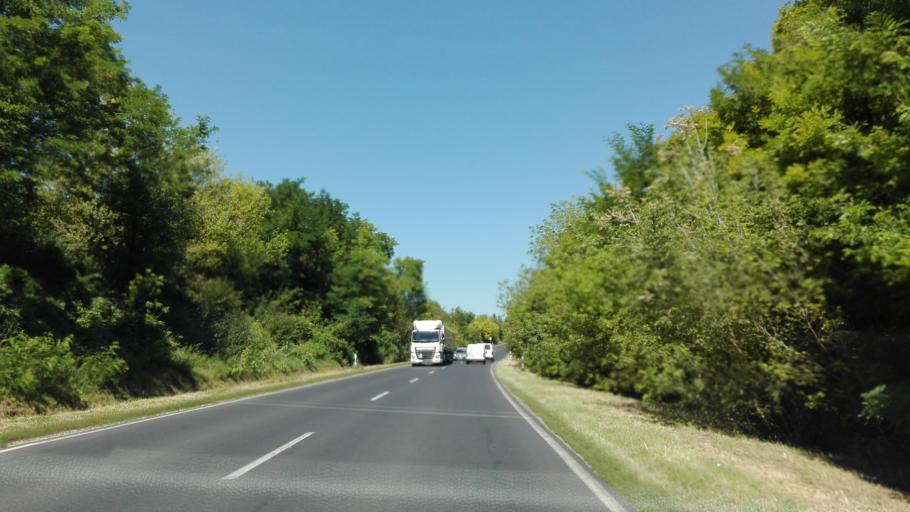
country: HU
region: Fejer
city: Mezoszilas
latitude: 46.7930
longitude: 18.4958
